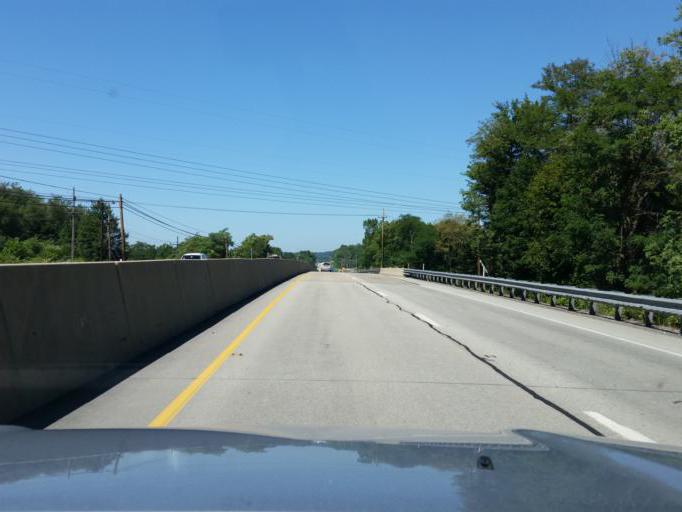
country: US
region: Pennsylvania
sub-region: Indiana County
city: Blairsville
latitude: 40.4407
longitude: -79.2496
